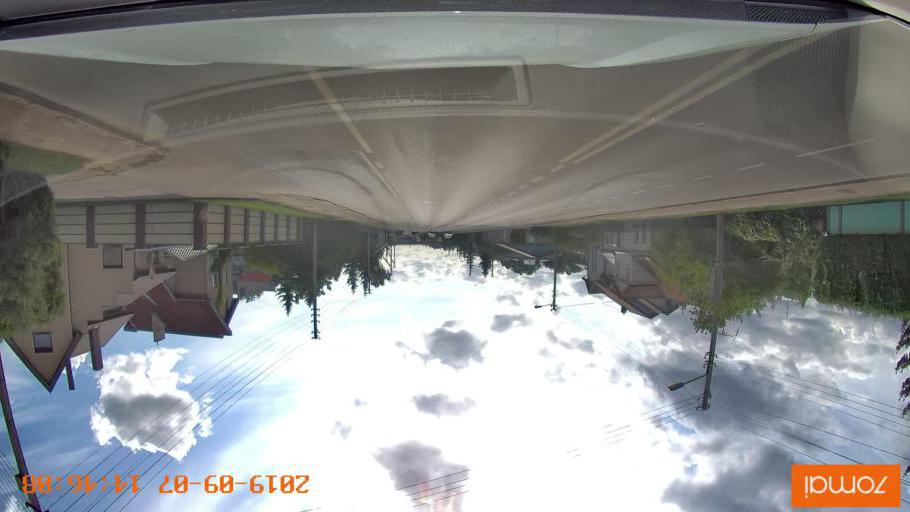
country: LT
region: Kauno apskritis
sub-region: Kaunas
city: Silainiai
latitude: 54.9279
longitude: 23.9061
